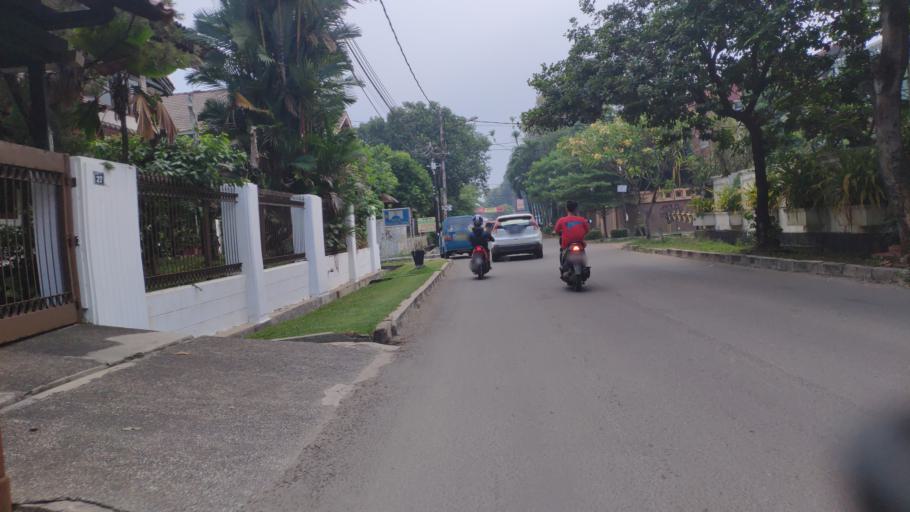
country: ID
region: West Java
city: Pamulang
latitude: -6.3461
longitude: 106.7794
